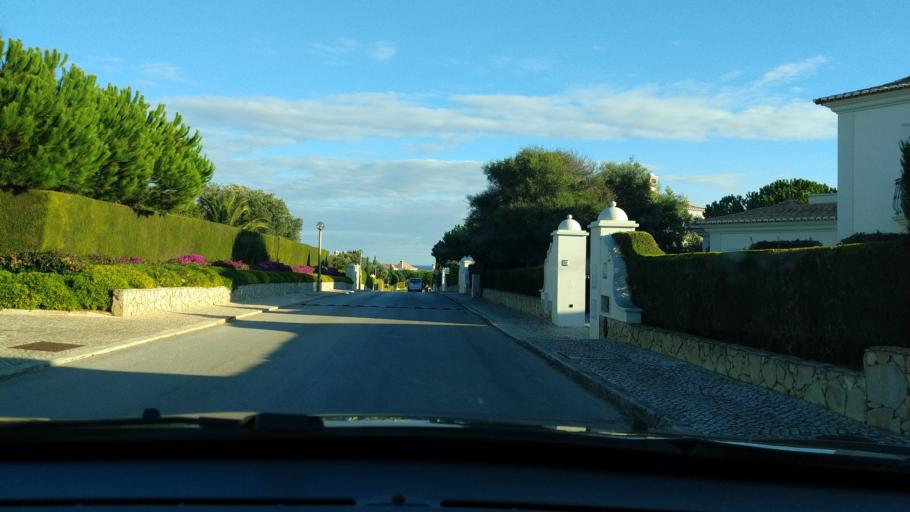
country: PT
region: Faro
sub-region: Vila do Bispo
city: Sagres
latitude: 37.0243
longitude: -8.9298
